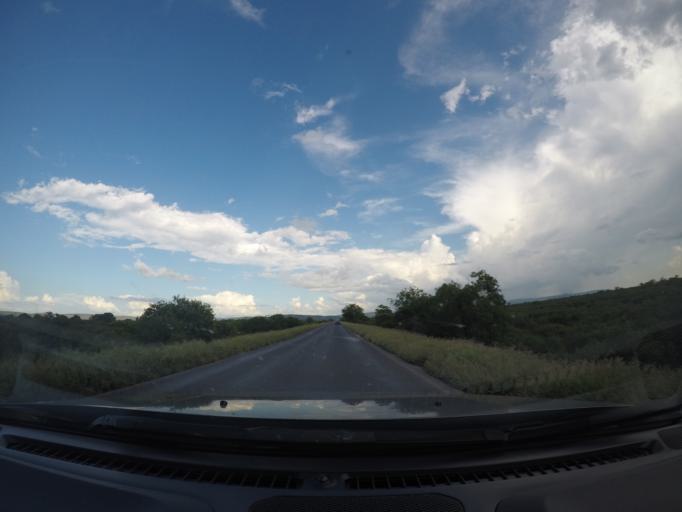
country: BR
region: Bahia
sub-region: Ibotirama
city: Ibotirama
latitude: -12.1740
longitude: -43.2562
